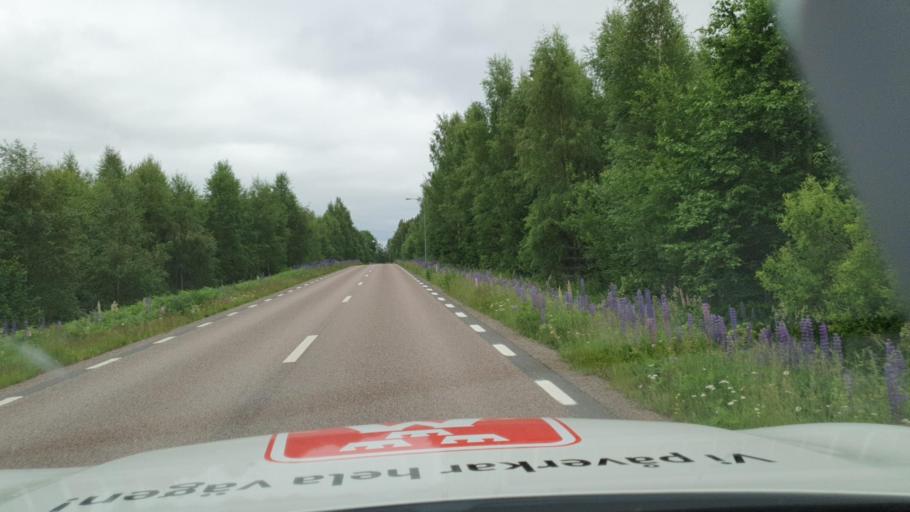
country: SE
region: Vaermland
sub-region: Sunne Kommun
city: Sunne
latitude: 59.8795
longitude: 12.9294
